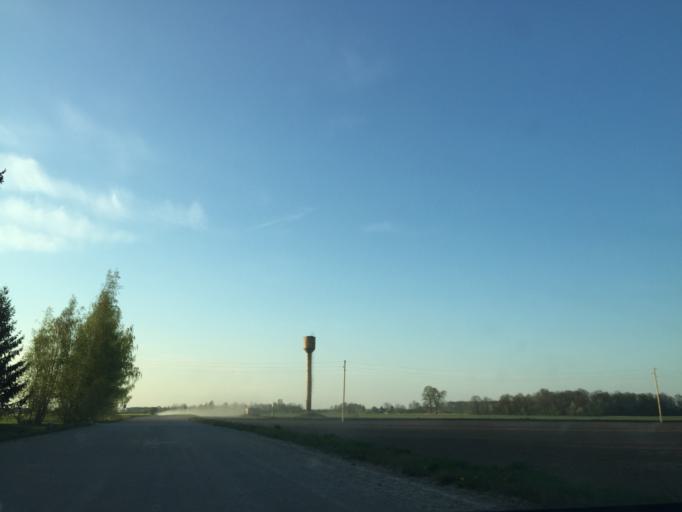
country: LV
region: Bauskas Rajons
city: Bauska
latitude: 56.3297
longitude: 24.1955
